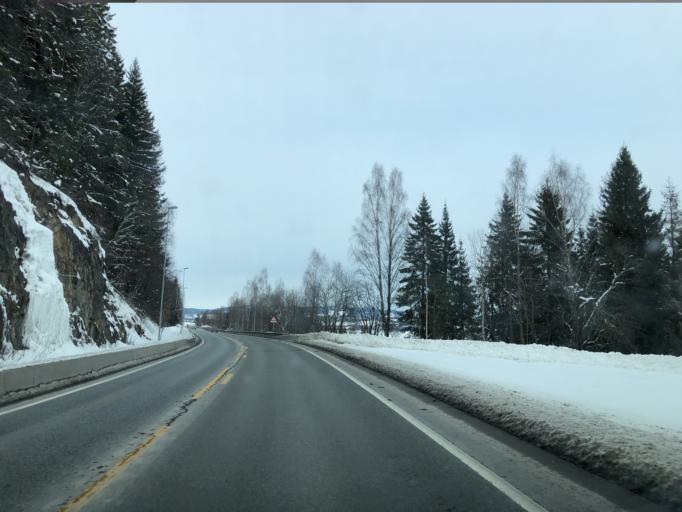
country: NO
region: Oppland
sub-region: Gjovik
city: Gjovik
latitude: 60.8429
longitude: 10.6853
